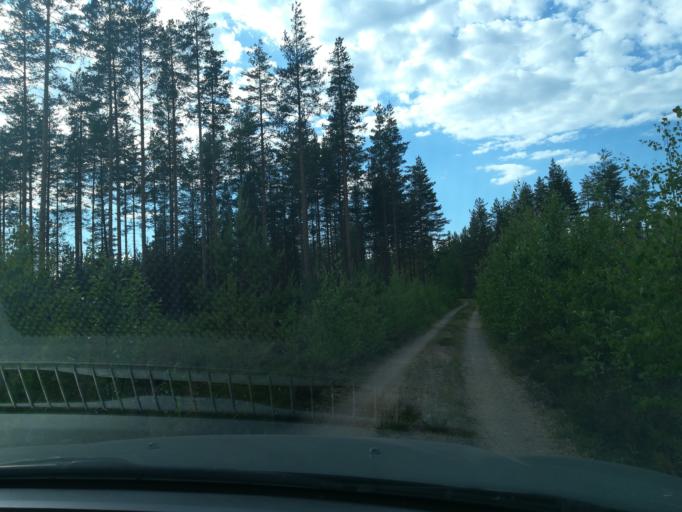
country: FI
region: Southern Savonia
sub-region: Savonlinna
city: Savonlinna
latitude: 61.6429
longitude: 28.7172
